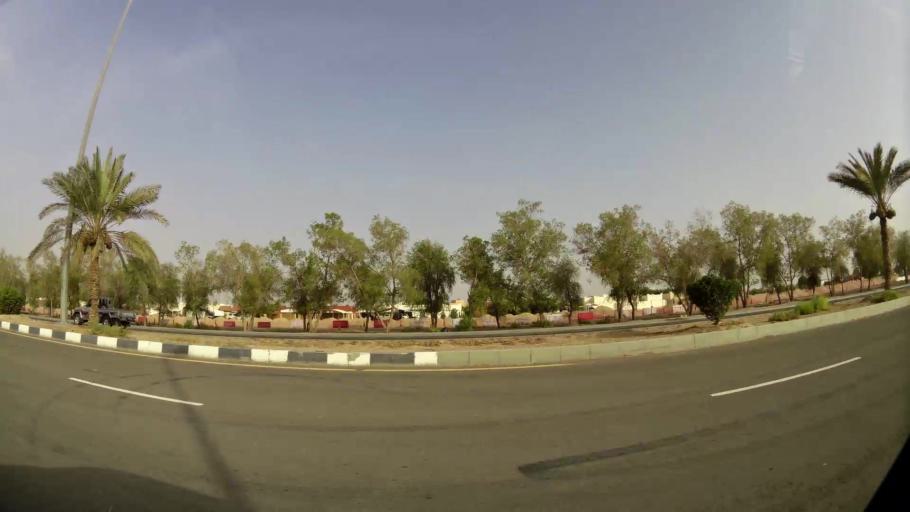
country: AE
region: Abu Dhabi
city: Al Ain
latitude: 24.1112
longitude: 55.6994
